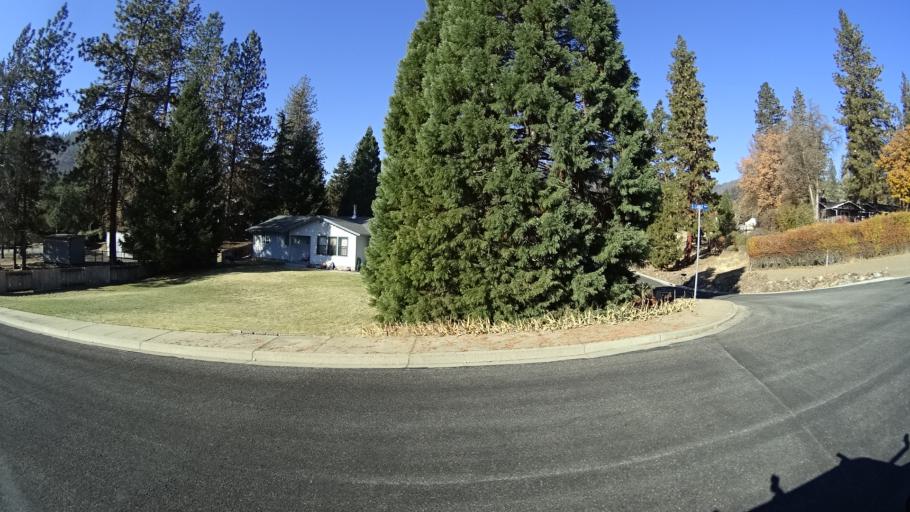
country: US
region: California
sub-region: Siskiyou County
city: Yreka
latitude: 41.7340
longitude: -122.6537
